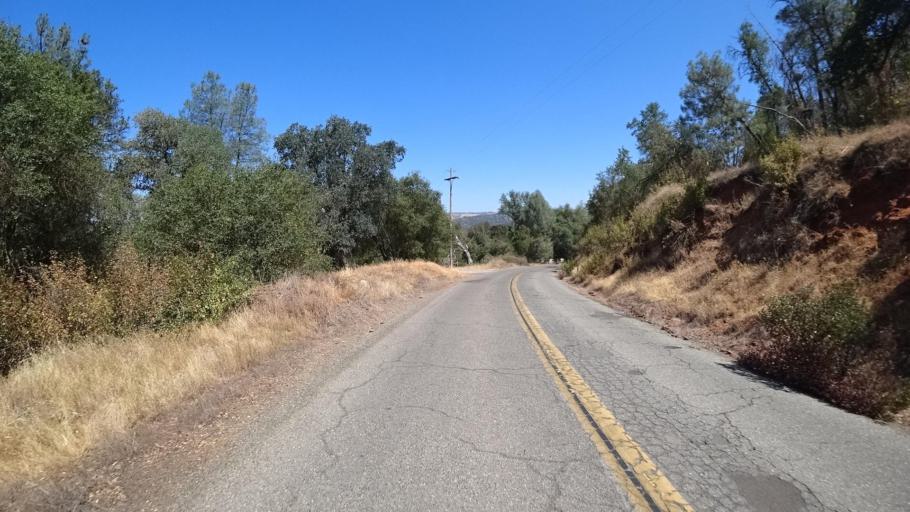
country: US
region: California
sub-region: Mariposa County
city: Mariposa
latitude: 37.4165
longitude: -119.9655
